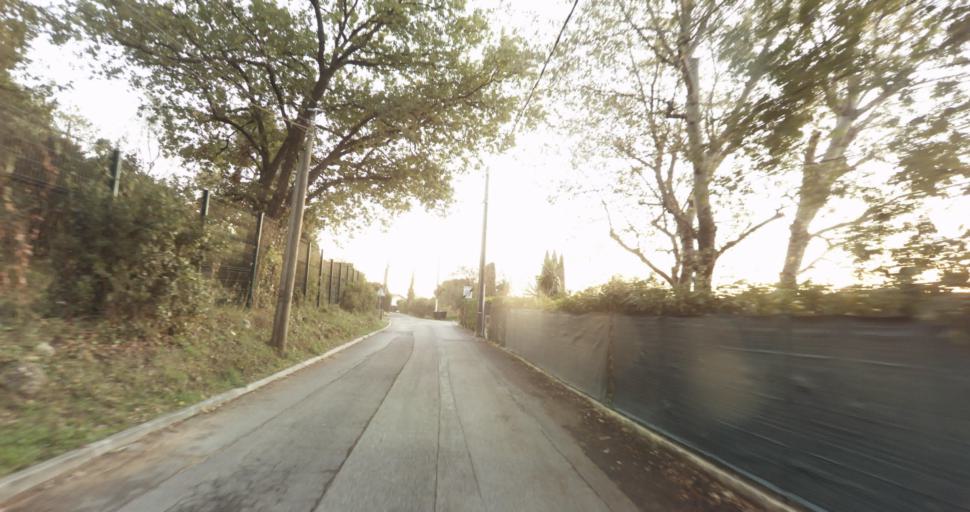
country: FR
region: Provence-Alpes-Cote d'Azur
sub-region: Departement des Alpes-Maritimes
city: La Gaude
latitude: 43.7254
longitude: 7.1334
